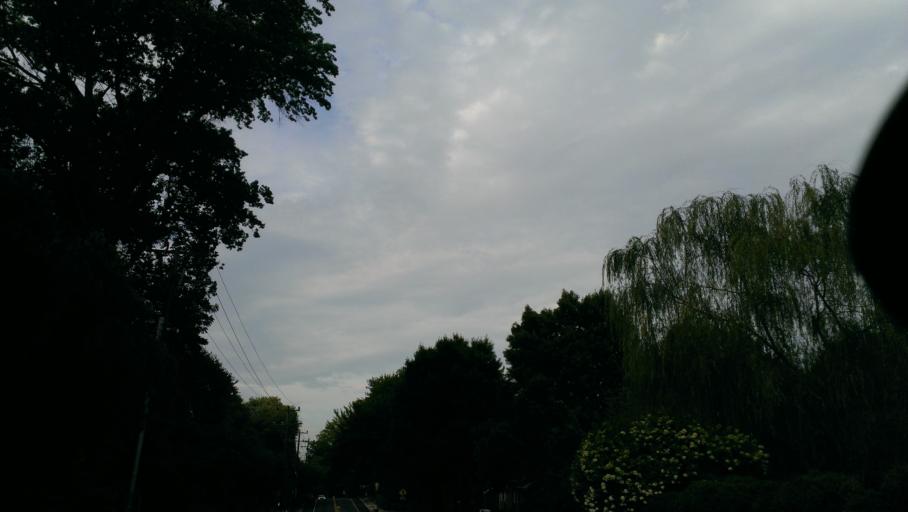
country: US
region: Virginia
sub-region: City of Falls Church
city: Falls Church
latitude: 38.8886
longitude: -77.1895
